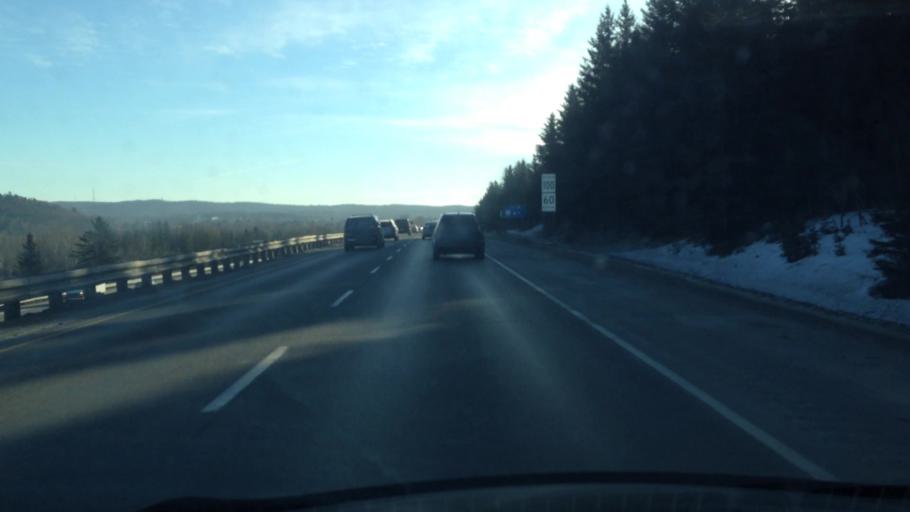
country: CA
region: Quebec
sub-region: Laurentides
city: Prevost
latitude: 45.8800
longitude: -74.0988
